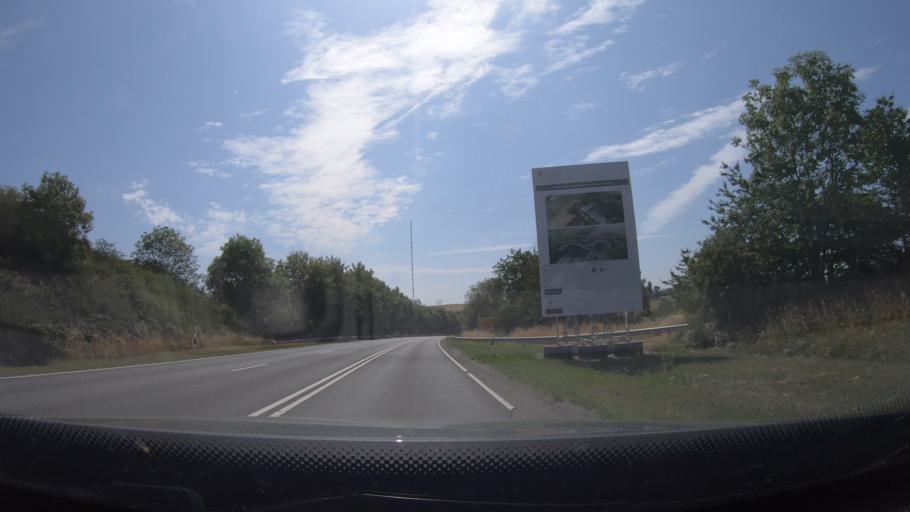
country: LU
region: Diekirch
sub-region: Canton de Clervaux
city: Hosingen
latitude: 50.0284
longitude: 6.0873
